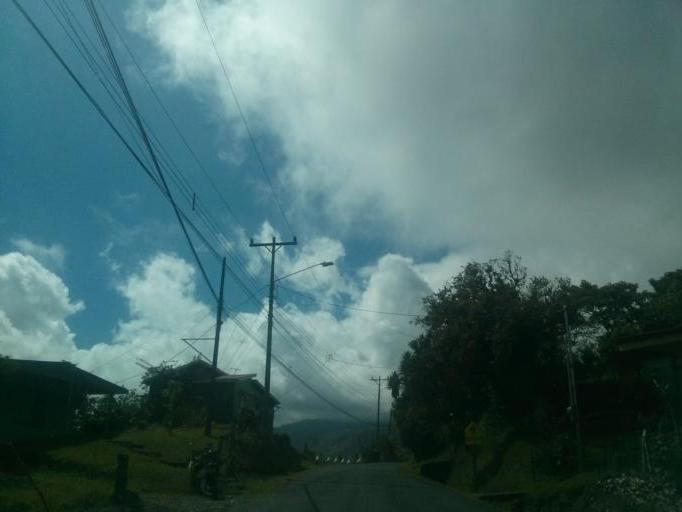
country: CR
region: Cartago
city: Turrialba
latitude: 9.9569
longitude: -83.7150
